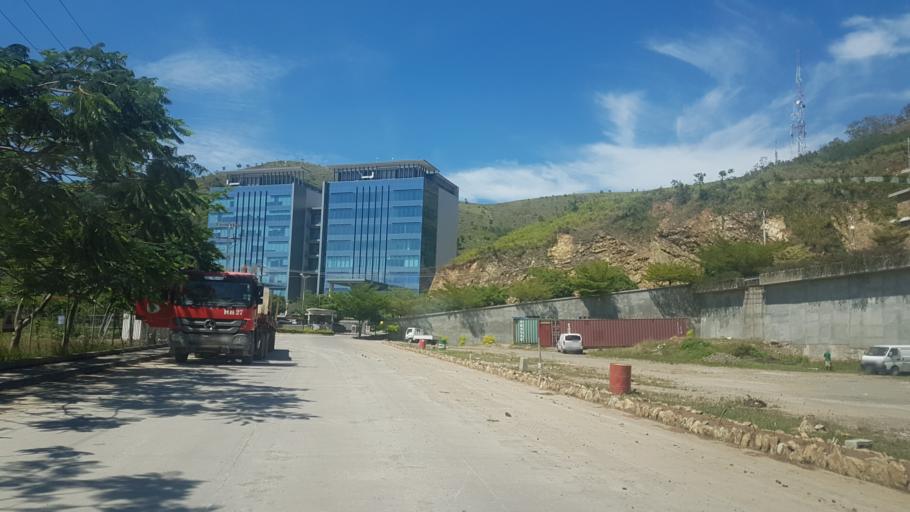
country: PG
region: National Capital
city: Port Moresby
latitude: -9.4392
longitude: 147.1783
